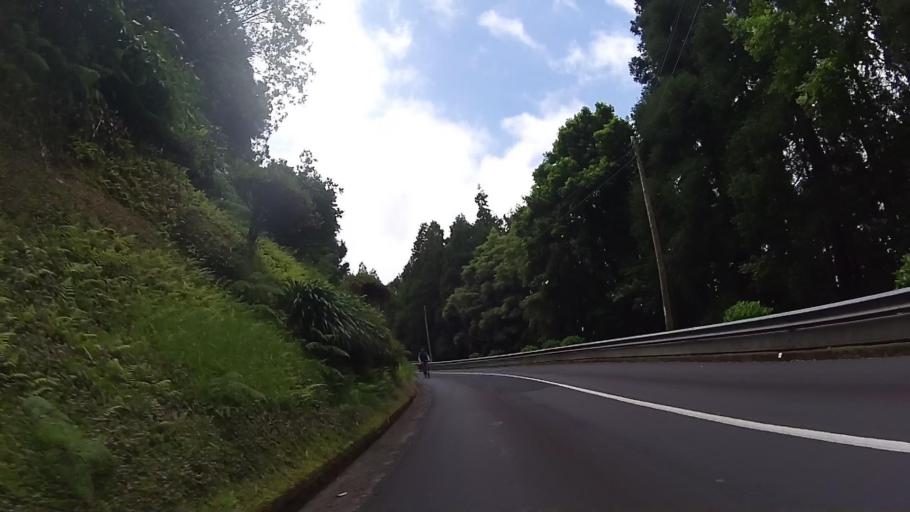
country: PT
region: Azores
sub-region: Povoacao
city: Furnas
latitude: 37.7646
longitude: -25.2884
